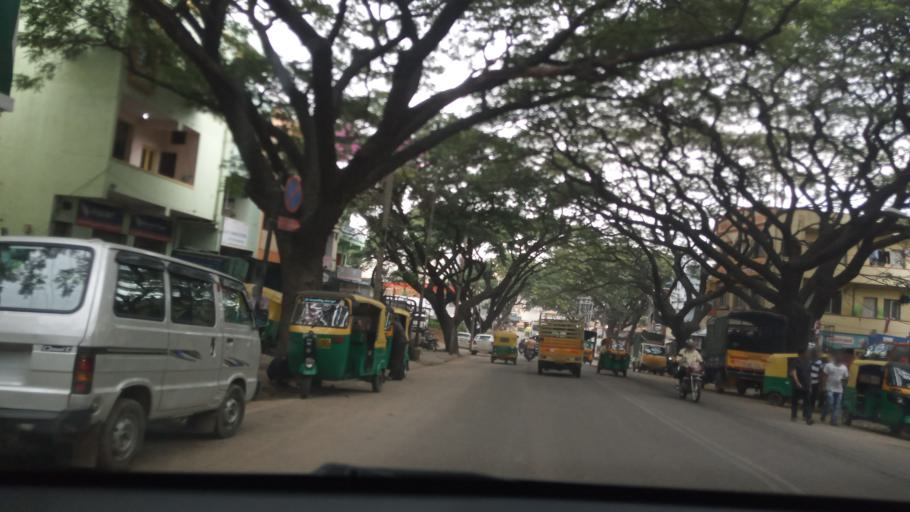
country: IN
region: Karnataka
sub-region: Bangalore Urban
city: Bangalore
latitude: 13.0204
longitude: 77.5374
